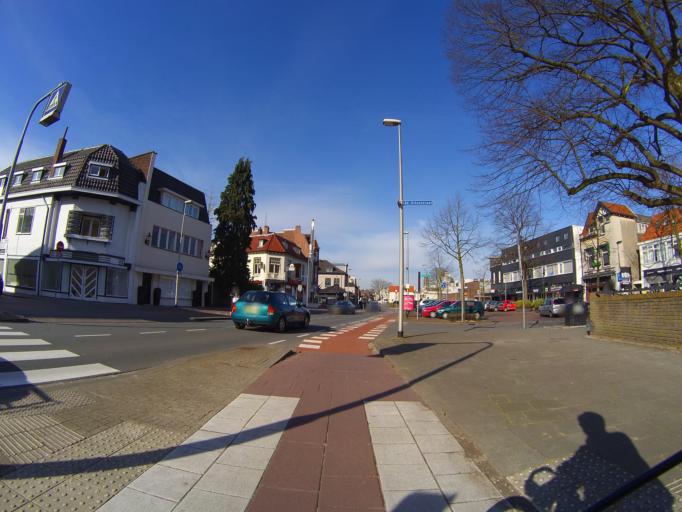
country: NL
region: North Holland
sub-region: Gemeente Bussum
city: Bussum
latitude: 52.2727
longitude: 5.1630
